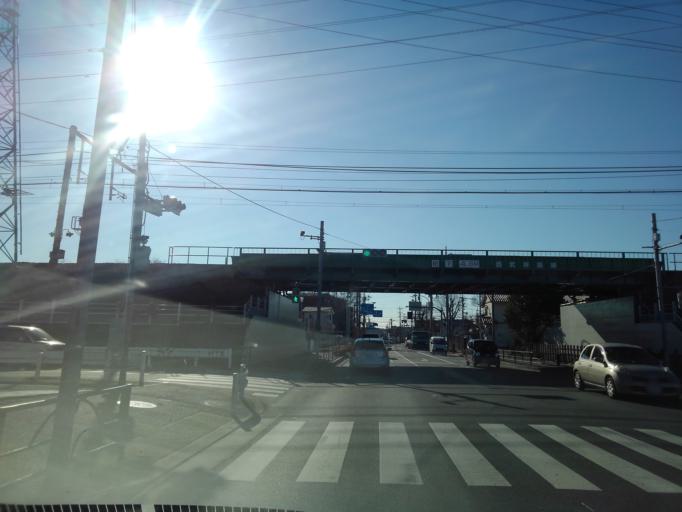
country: JP
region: Tokyo
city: Hino
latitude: 35.7282
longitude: 139.3825
